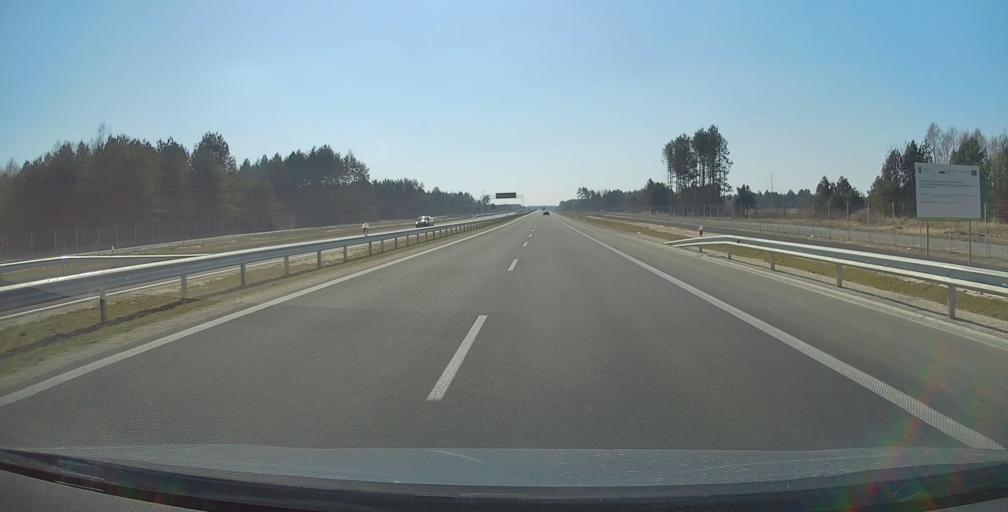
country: PL
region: Subcarpathian Voivodeship
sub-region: Powiat nizanski
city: Konczyce
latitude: 50.4589
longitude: 22.1406
